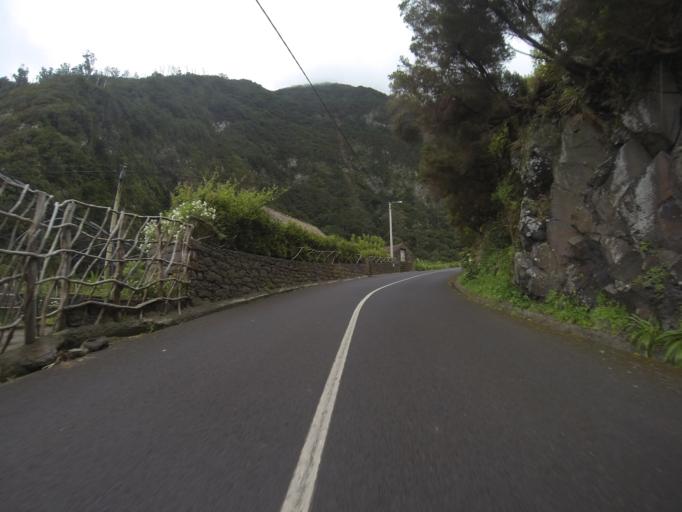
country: PT
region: Madeira
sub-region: Porto Moniz
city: Porto Moniz
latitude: 32.8168
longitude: -17.1094
